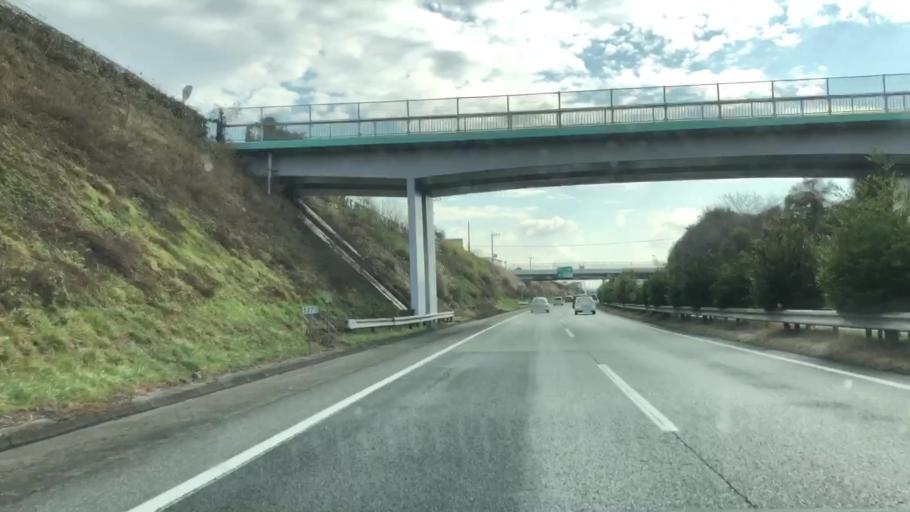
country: JP
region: Fukuoka
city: Setakamachi-takayanagi
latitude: 33.1335
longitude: 130.5168
